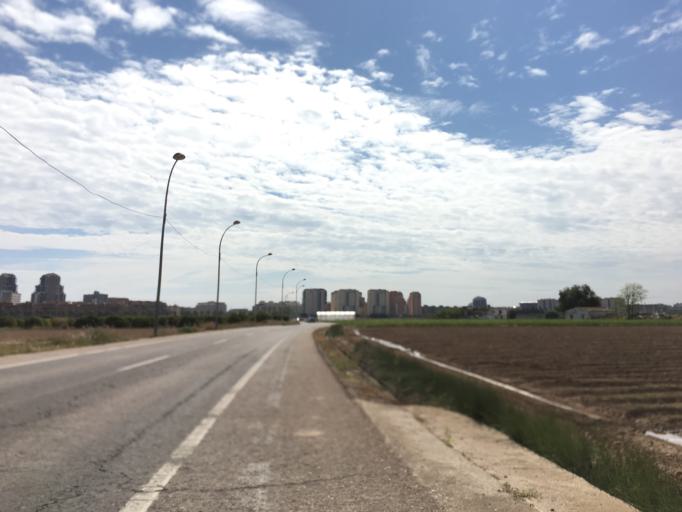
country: ES
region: Valencia
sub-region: Provincia de Valencia
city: Mislata
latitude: 39.4900
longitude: -0.4144
